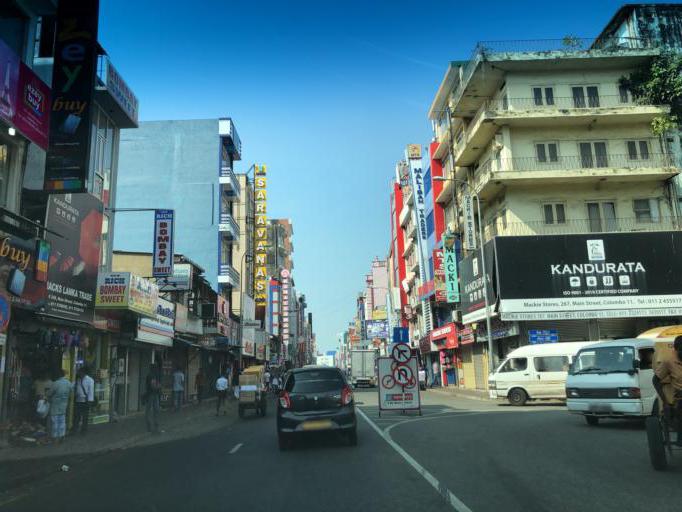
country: LK
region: Western
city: Colombo
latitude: 6.9386
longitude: 79.8531
